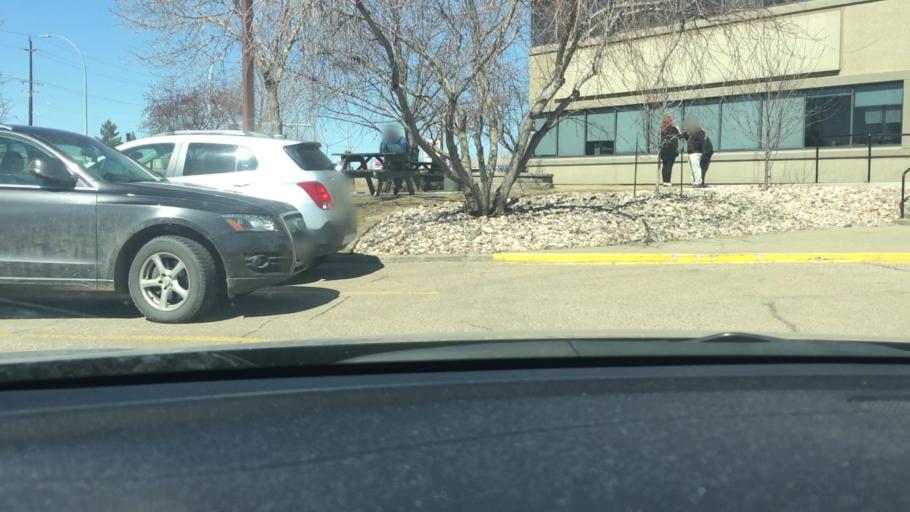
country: CA
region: Alberta
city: Edmonton
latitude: 53.5366
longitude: -113.4178
